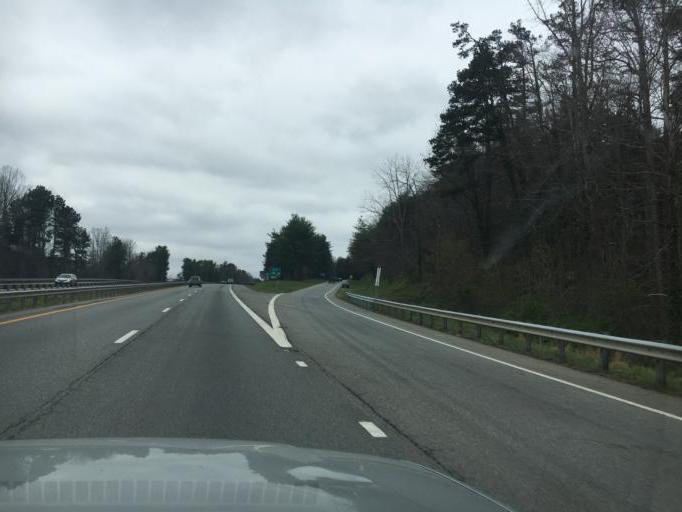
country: US
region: North Carolina
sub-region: Buncombe County
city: Weaverville
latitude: 35.7182
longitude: -82.5595
